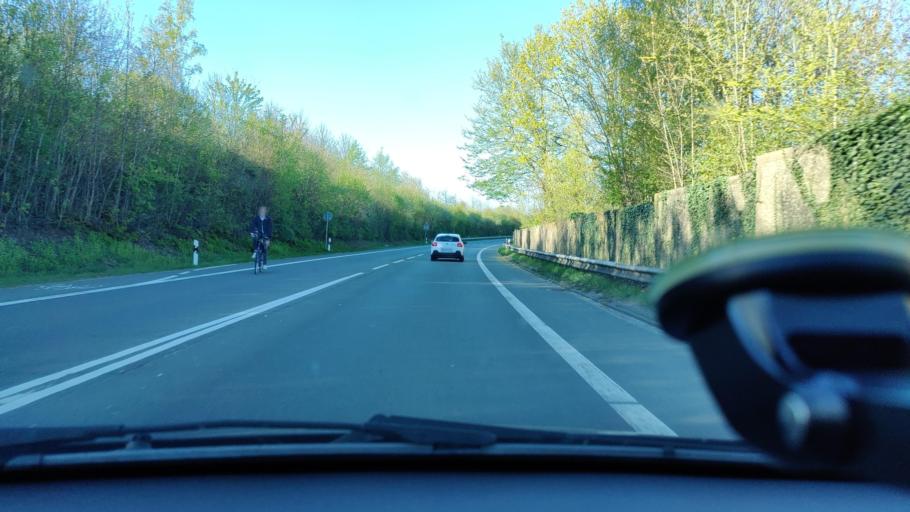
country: DE
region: North Rhine-Westphalia
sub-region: Regierungsbezirk Munster
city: Coesfeld
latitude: 51.9477
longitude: 7.1497
